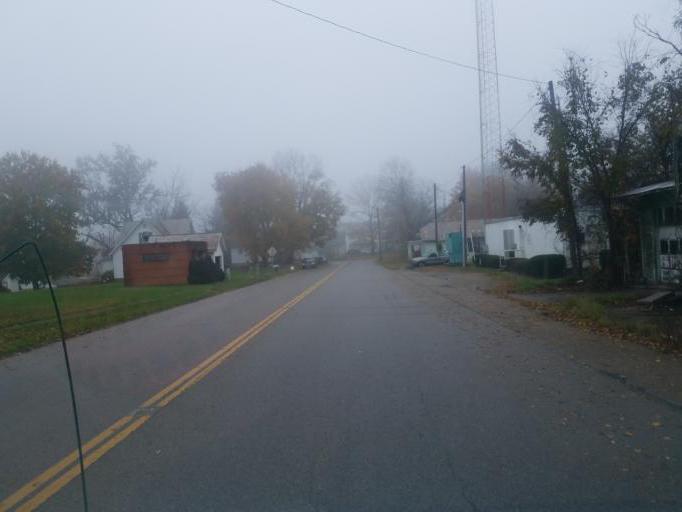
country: US
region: Ohio
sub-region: Morgan County
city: McConnelsville
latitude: 39.5740
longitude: -81.8525
